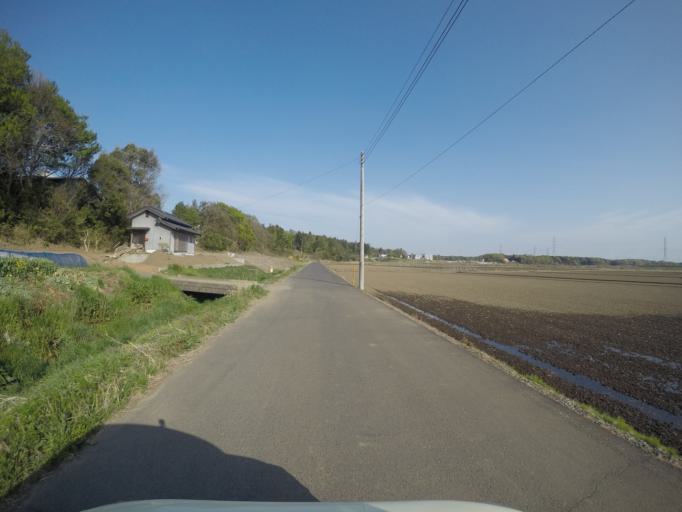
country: JP
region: Ibaraki
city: Ishige
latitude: 36.1851
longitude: 140.0133
